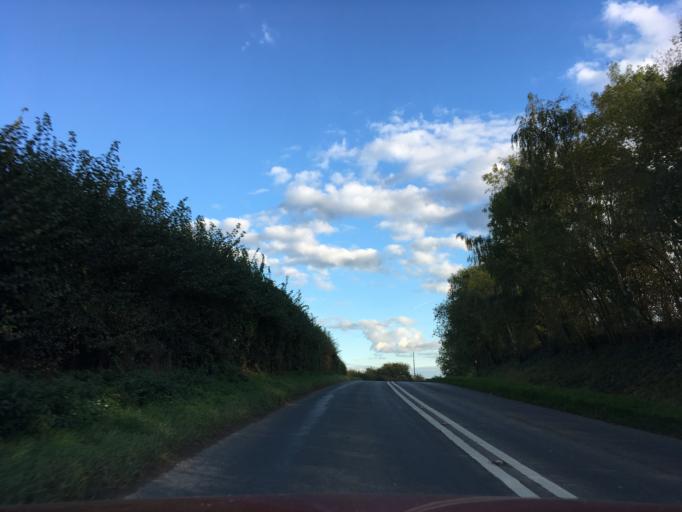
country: GB
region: England
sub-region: Herefordshire
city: Ledbury
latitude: 52.0429
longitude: -2.4009
